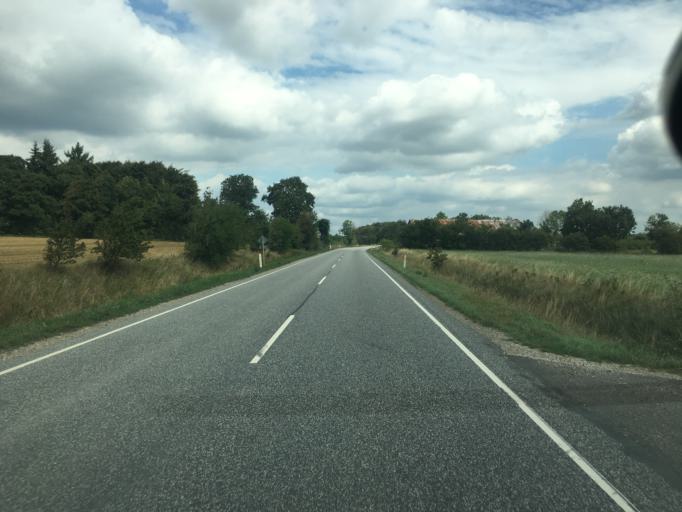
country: DK
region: South Denmark
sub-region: Aabenraa Kommune
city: Rodekro
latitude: 54.9799
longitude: 9.3360
